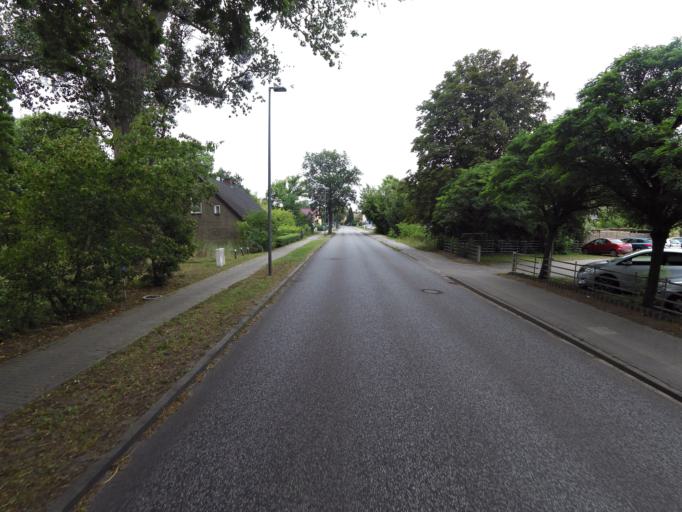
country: DE
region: Brandenburg
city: Zehdenick
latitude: 52.9786
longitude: 13.3500
